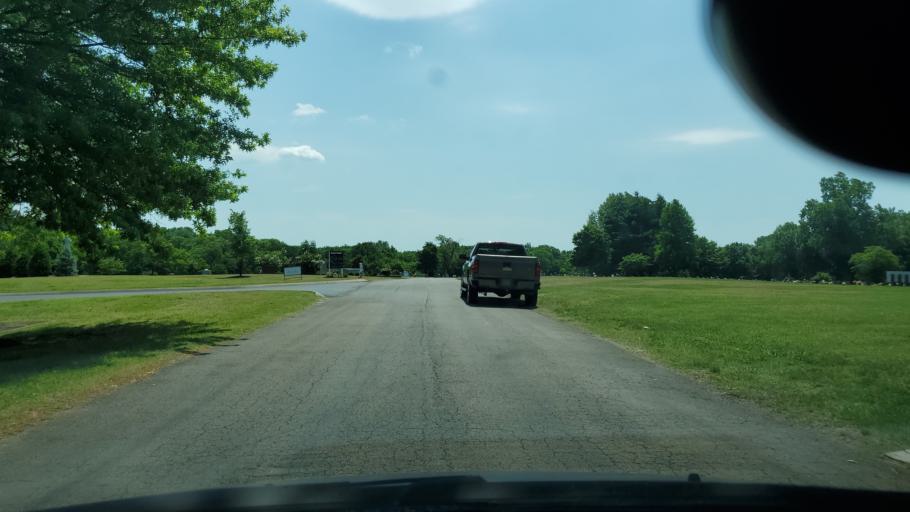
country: US
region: Tennessee
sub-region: Davidson County
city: Goodlettsville
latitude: 36.2424
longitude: -86.7210
